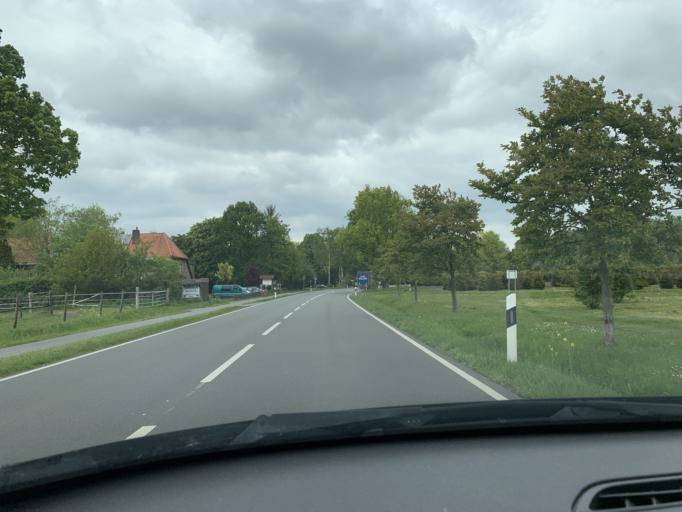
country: DE
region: Lower Saxony
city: Bad Zwischenahn
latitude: 53.2045
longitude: 8.0403
